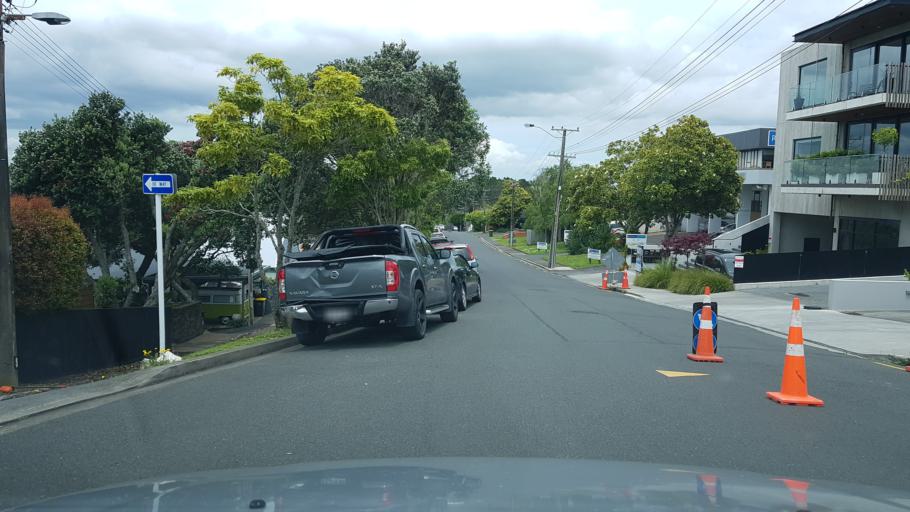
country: NZ
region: Auckland
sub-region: Auckland
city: North Shore
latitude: -36.8134
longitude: 174.7261
